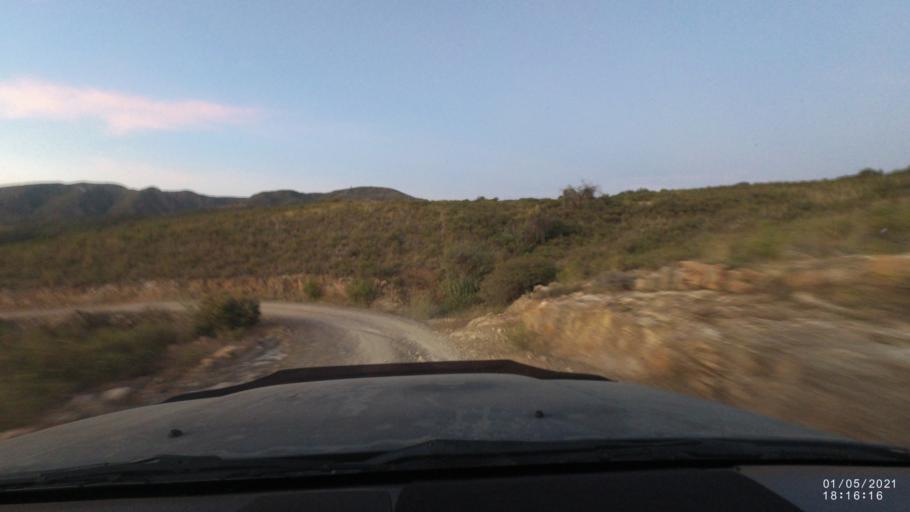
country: BO
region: Cochabamba
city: Capinota
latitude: -17.6723
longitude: -66.2176
